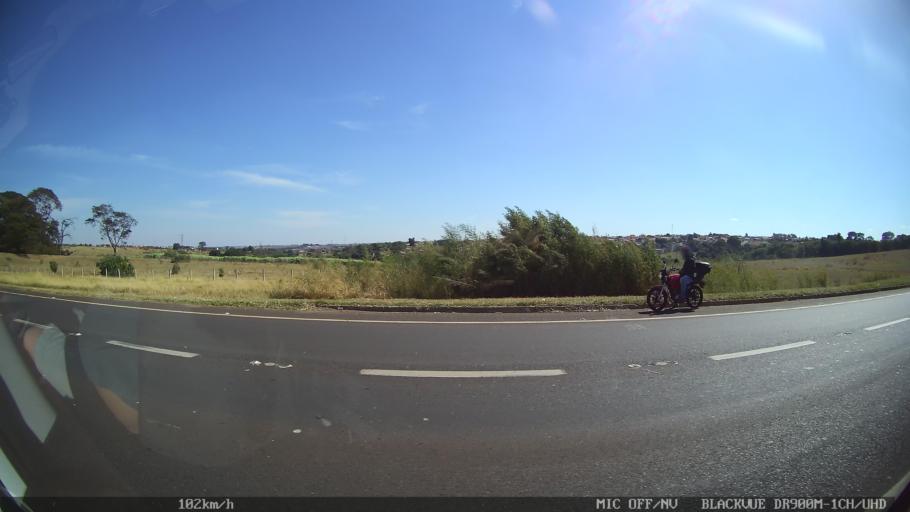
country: BR
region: Sao Paulo
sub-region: Franca
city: Franca
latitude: -20.5173
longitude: -47.4165
